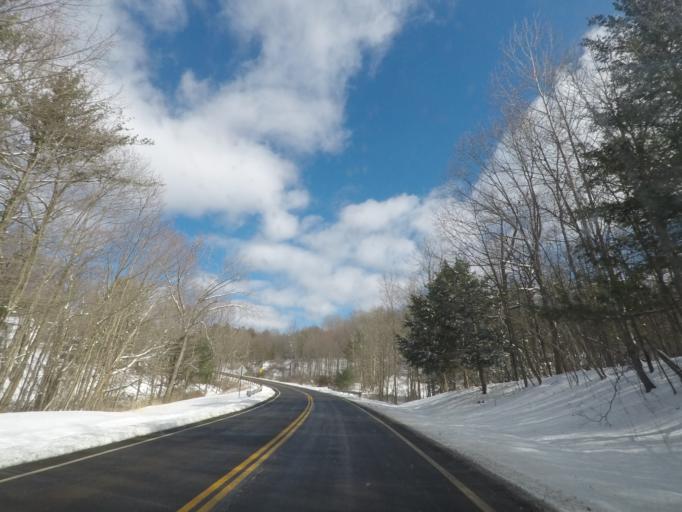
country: US
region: New York
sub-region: Rensselaer County
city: Nassau
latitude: 42.4696
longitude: -73.5281
